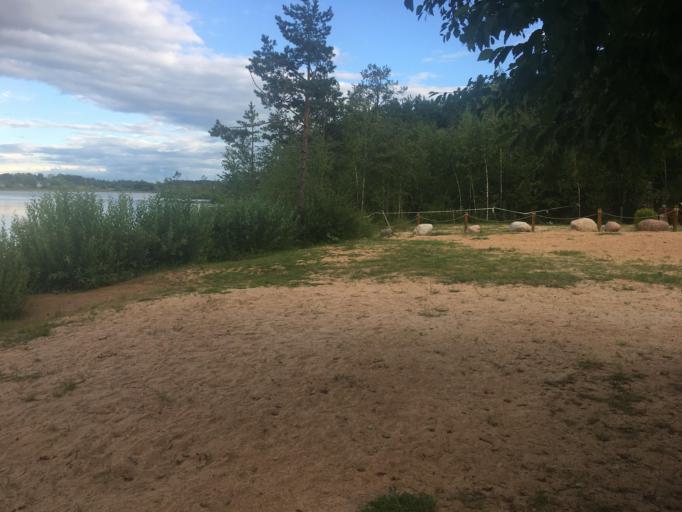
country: RU
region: Pskov
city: Izborsk
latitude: 57.8291
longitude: 27.9545
